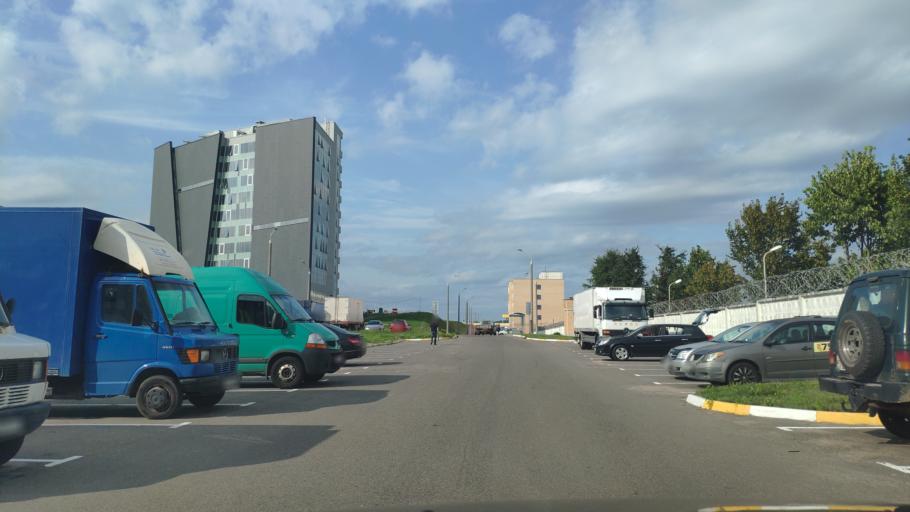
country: BY
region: Minsk
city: Vyaliki Trastsyanets
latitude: 53.8625
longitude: 27.6882
